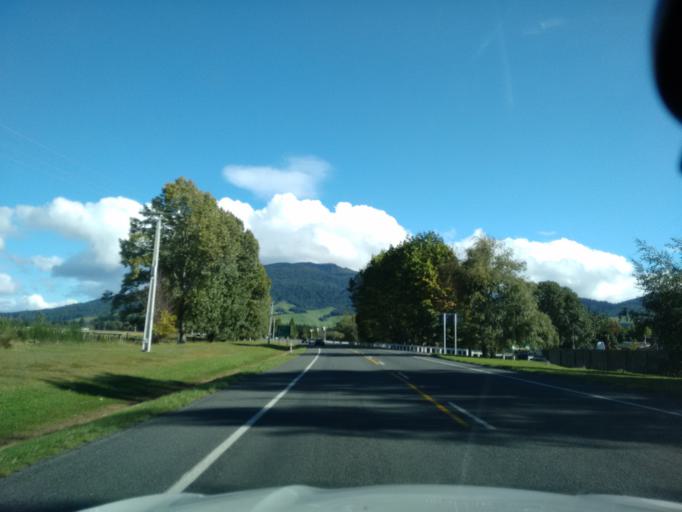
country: NZ
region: Waikato
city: Turangi
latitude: -38.9940
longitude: 175.8065
